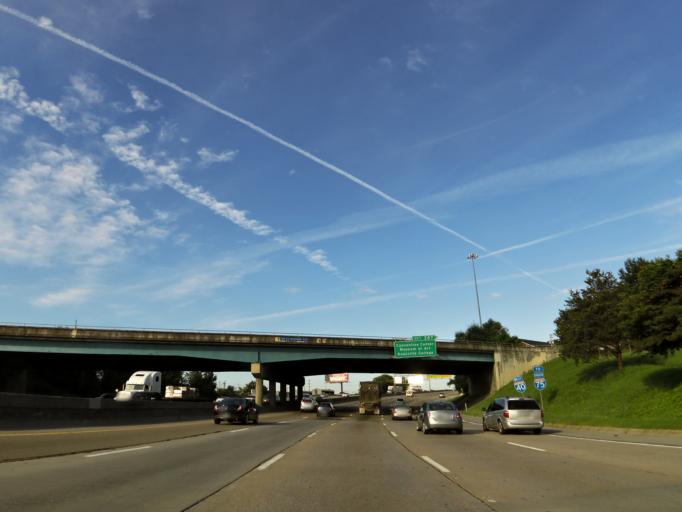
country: US
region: Tennessee
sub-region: Knox County
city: Knoxville
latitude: 35.9662
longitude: -83.9323
